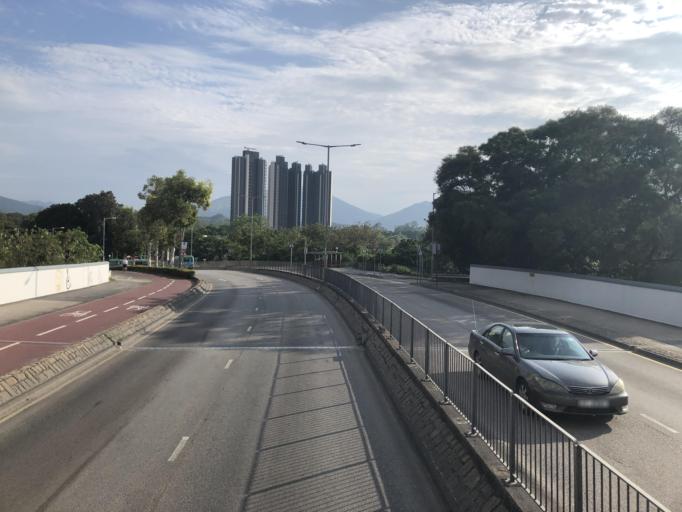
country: CN
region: Guangdong
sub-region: Shenzhen
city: Shenzhen
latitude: 22.5047
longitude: 114.1241
